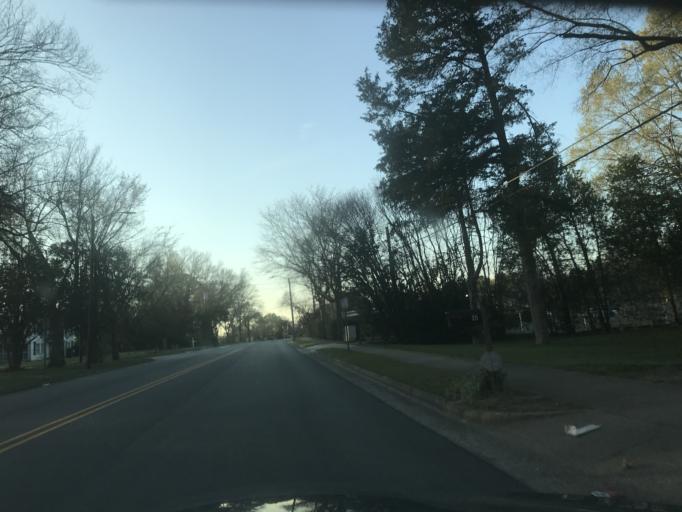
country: US
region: North Carolina
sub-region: Wake County
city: Raleigh
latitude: 35.7777
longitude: -78.6066
